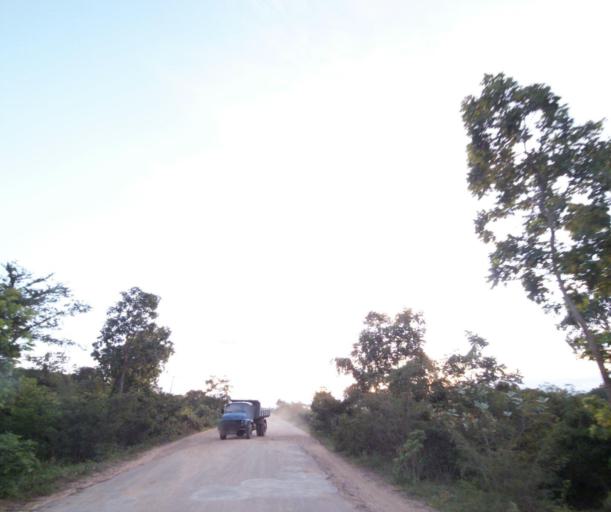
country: BR
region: Bahia
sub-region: Sao Felix Do Coribe
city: Santa Maria da Vitoria
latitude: -13.6338
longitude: -44.4307
